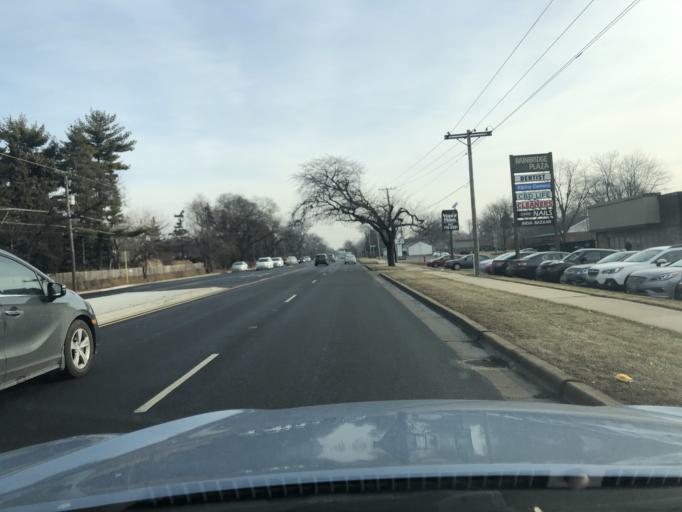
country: US
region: Illinois
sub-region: Cook County
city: Mount Prospect
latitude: 42.0476
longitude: -87.9371
